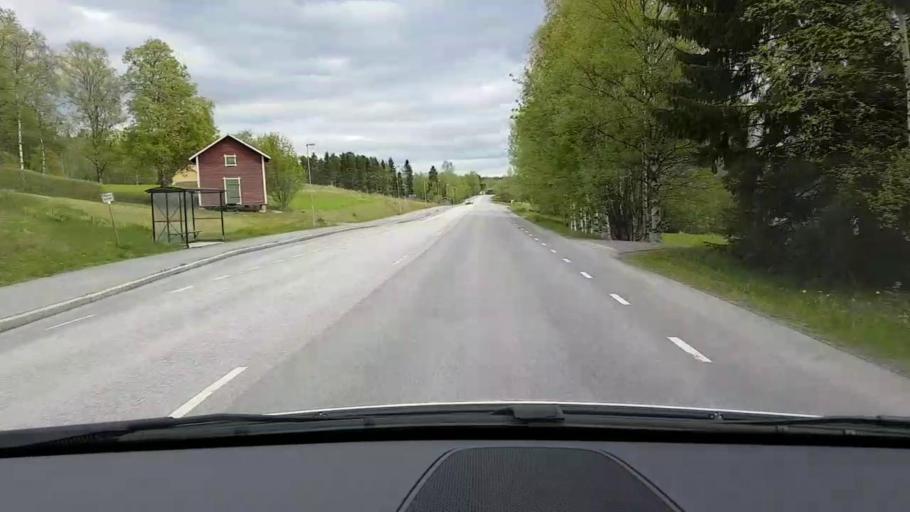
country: SE
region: Jaemtland
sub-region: OEstersunds Kommun
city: Brunflo
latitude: 63.1192
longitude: 14.7834
